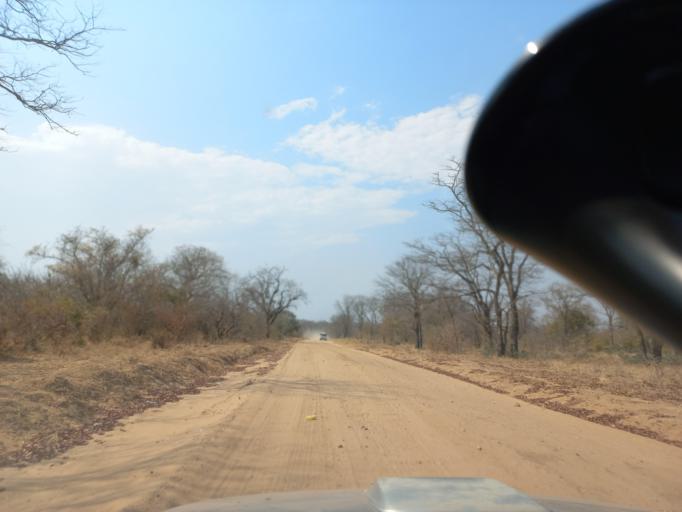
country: ZW
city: Chirundu
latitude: -15.9338
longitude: 28.9151
